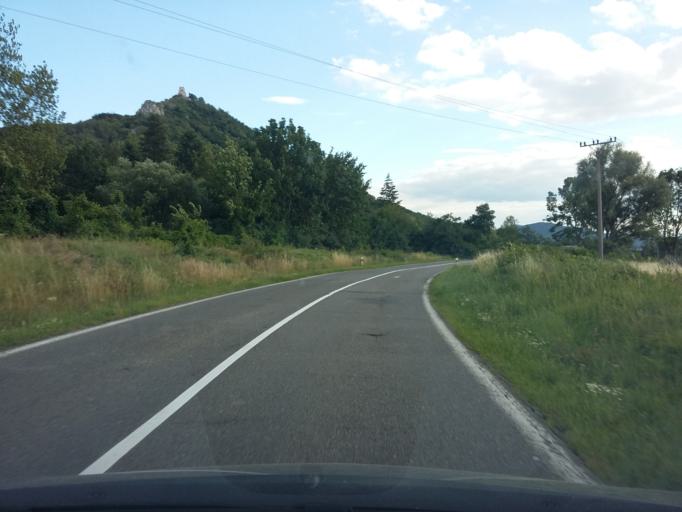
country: SK
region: Trnavsky
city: Smolenice
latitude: 48.5013
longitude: 17.2669
